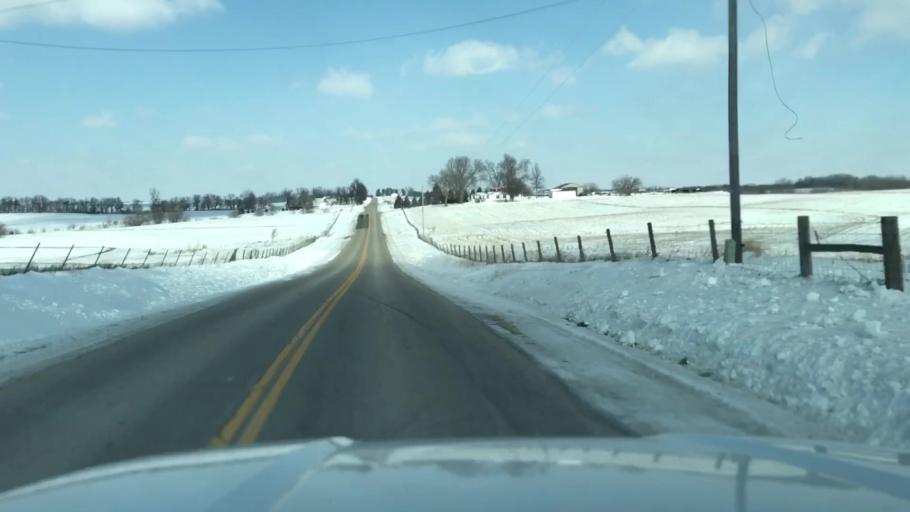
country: US
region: Missouri
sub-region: Nodaway County
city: Maryville
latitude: 40.3625
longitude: -94.7219
